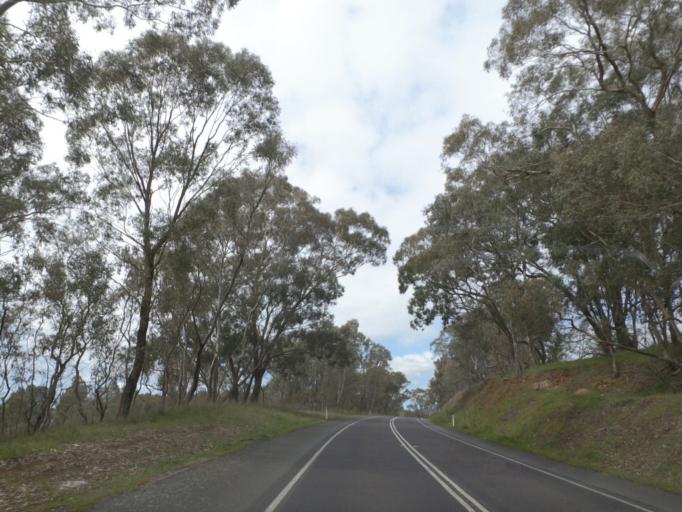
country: AU
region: Victoria
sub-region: Murrindindi
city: Kinglake West
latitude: -37.1590
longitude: 145.2900
